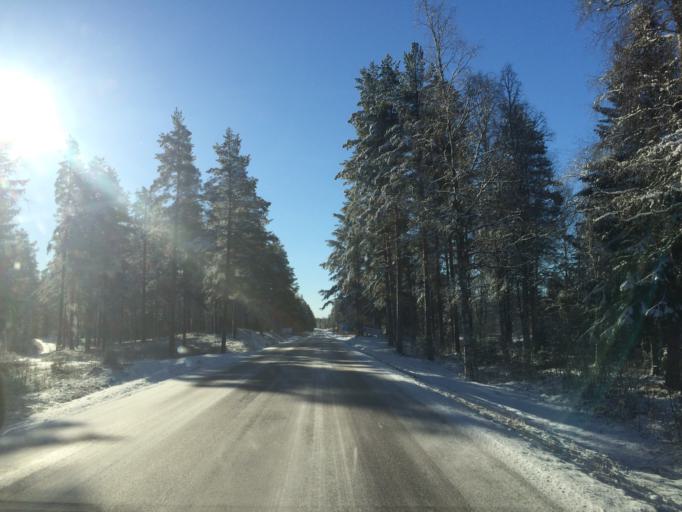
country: SE
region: Dalarna
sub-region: Vansbro Kommun
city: Vansbro
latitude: 60.8222
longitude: 14.1284
